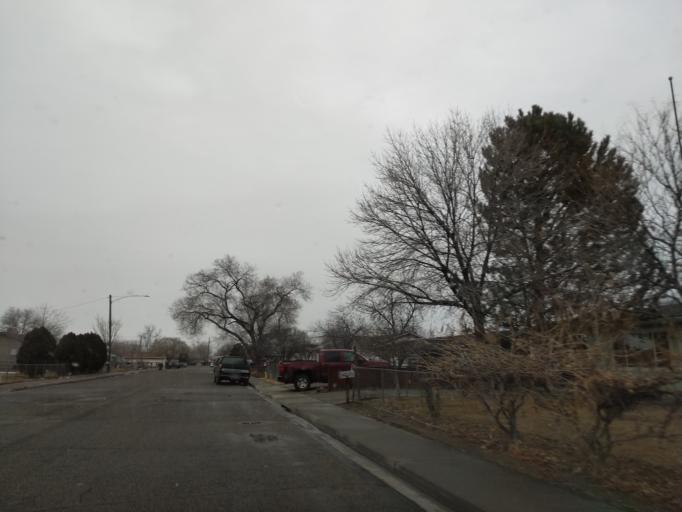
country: US
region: Colorado
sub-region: Mesa County
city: Fruitvale
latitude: 39.0746
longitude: -108.5223
